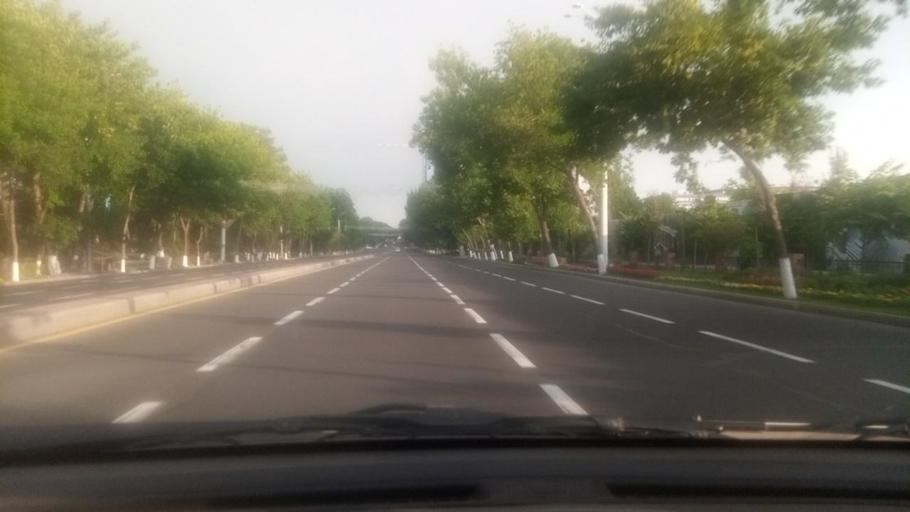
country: UZ
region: Toshkent
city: Salor
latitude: 41.3358
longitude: 69.3437
